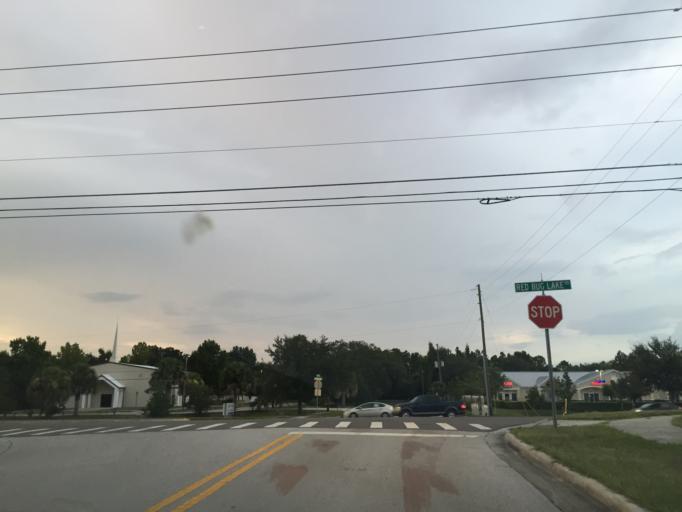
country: US
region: Florida
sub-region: Seminole County
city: Oviedo
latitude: 28.6476
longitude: -81.2467
